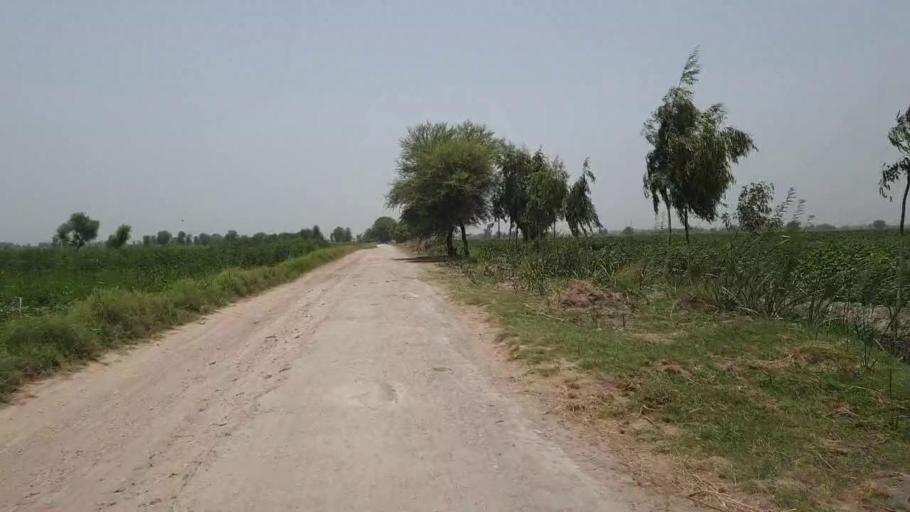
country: PK
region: Sindh
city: Tando Mittha Khan
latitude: 26.0693
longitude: 69.2148
